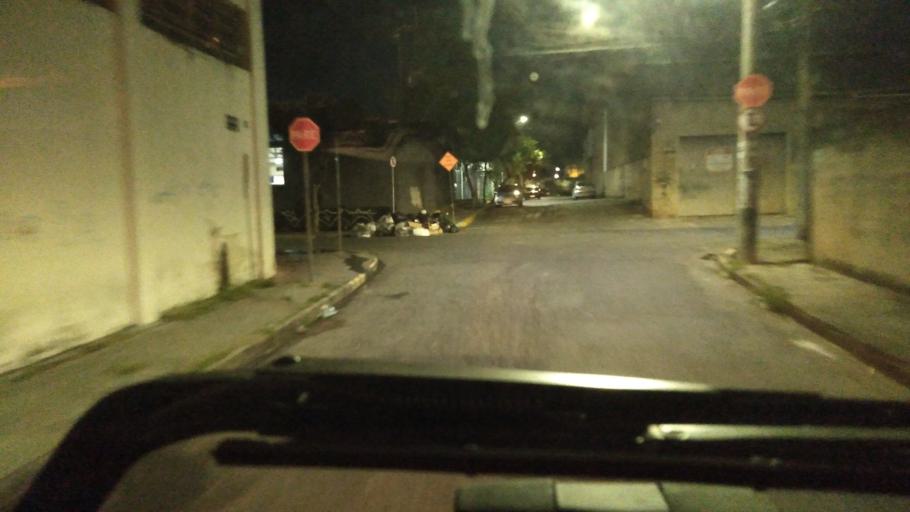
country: BR
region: Minas Gerais
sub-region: Belo Horizonte
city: Belo Horizonte
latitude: -19.9218
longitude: -43.9818
